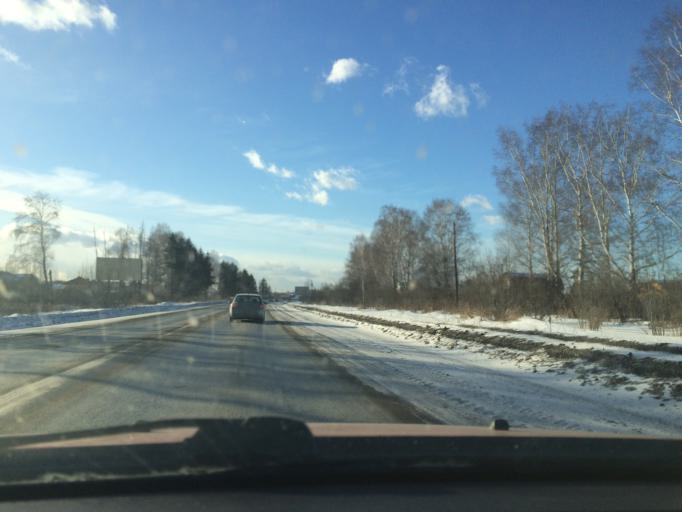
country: RU
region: Sverdlovsk
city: Istok
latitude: 56.7732
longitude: 60.8501
